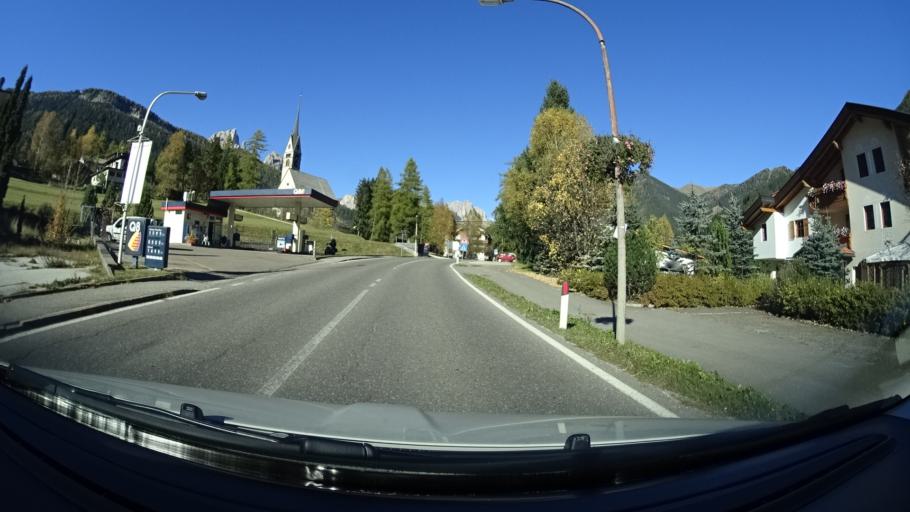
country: IT
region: Trentino-Alto Adige
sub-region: Provincia di Trento
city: Vigo di Fassa
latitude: 46.4193
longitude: 11.6808
